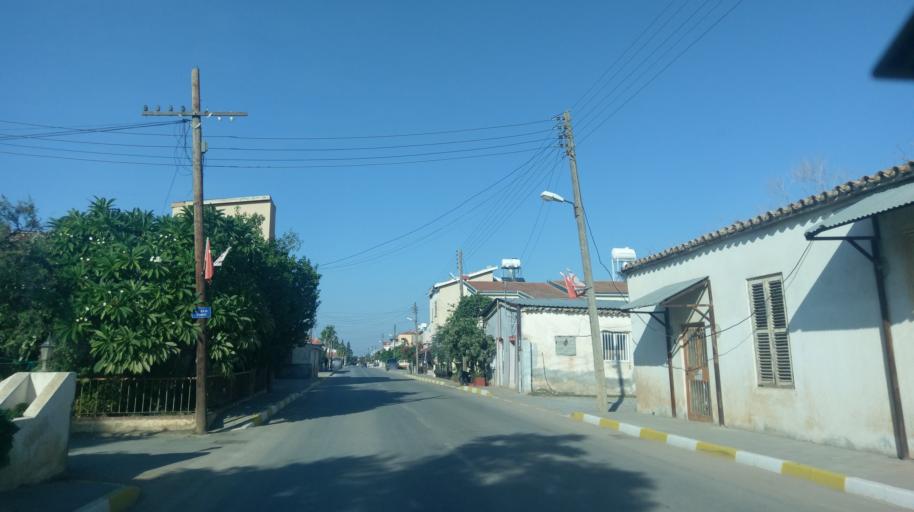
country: CY
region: Larnaka
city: Pergamos
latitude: 35.0427
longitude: 33.7081
